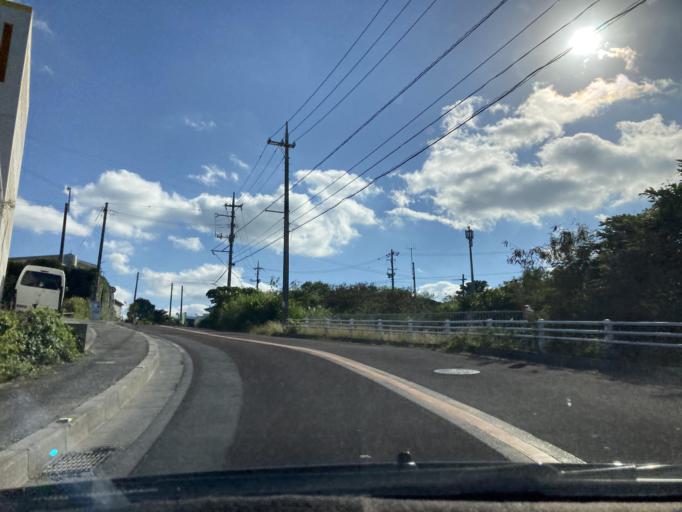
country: JP
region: Okinawa
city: Katsuren-haebaru
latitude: 26.3197
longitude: 127.9093
